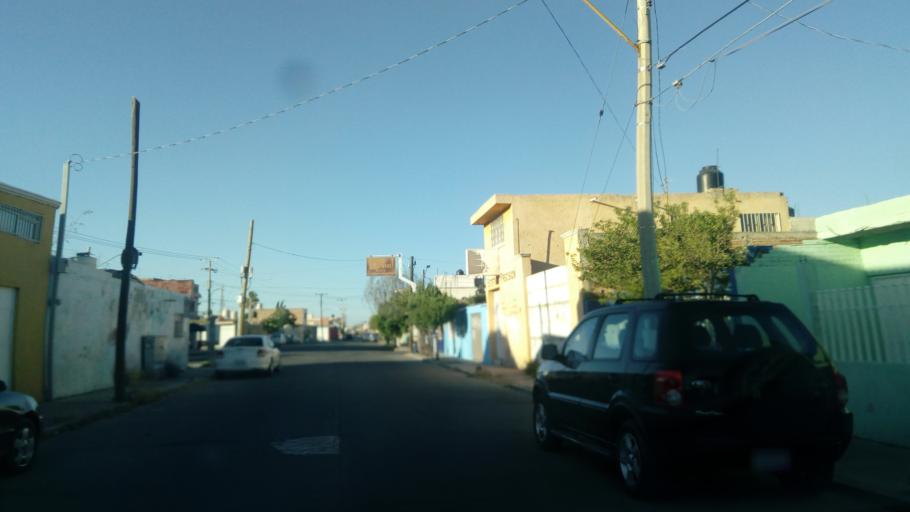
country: MX
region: Durango
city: Victoria de Durango
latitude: 24.0075
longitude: -104.6720
